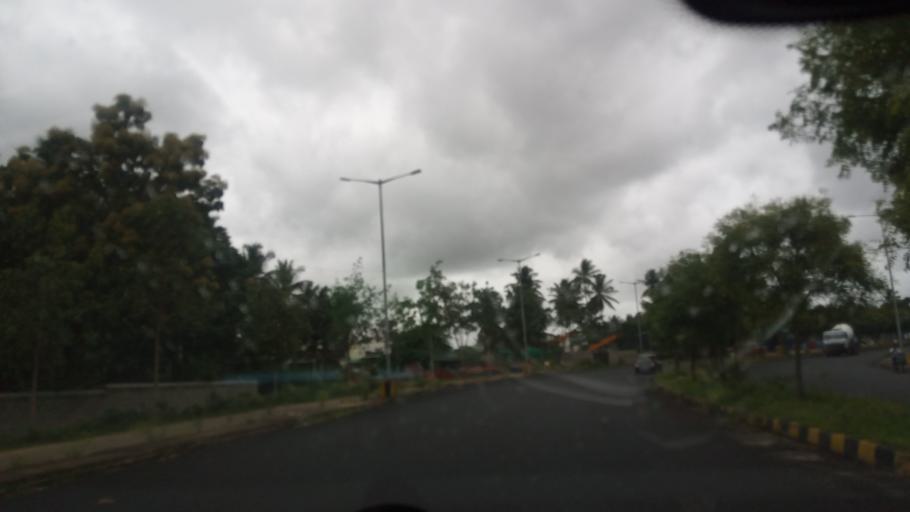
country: IN
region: Karnataka
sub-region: Mysore
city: Mysore
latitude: 12.3078
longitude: 76.5997
